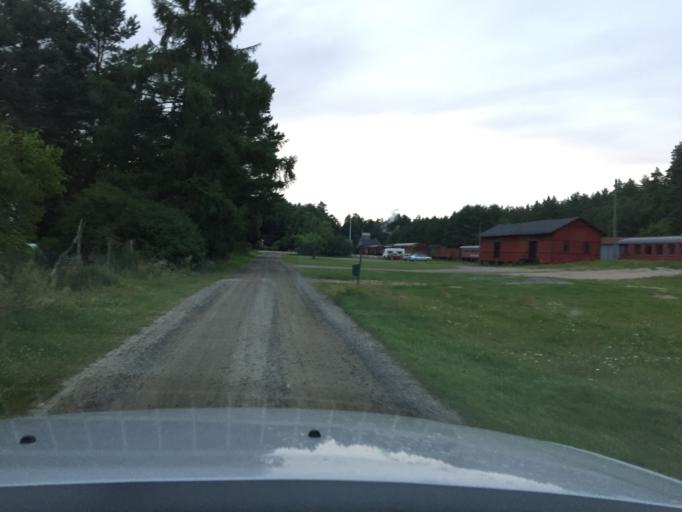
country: SE
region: Skane
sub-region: Kristianstads Kommun
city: Degeberga
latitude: 55.7334
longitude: 14.1246
